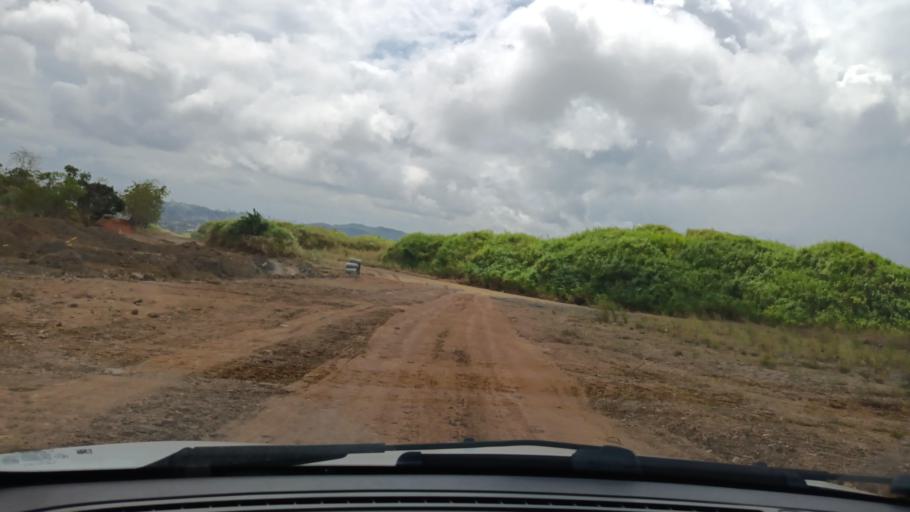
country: PA
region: Panama
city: La Cabima
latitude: 9.1139
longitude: -79.4984
